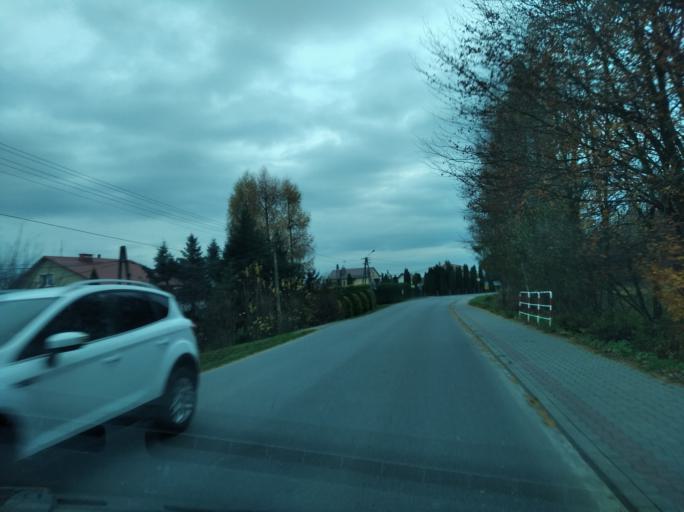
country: PL
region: Subcarpathian Voivodeship
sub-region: Powiat ropczycko-sedziszowski
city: Iwierzyce
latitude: 50.0272
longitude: 21.7565
